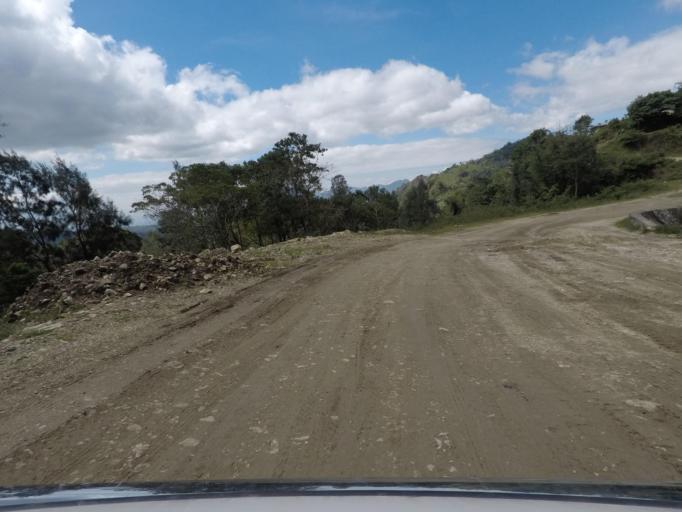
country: TL
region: Baucau
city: Venilale
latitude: -8.7170
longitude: 126.3665
